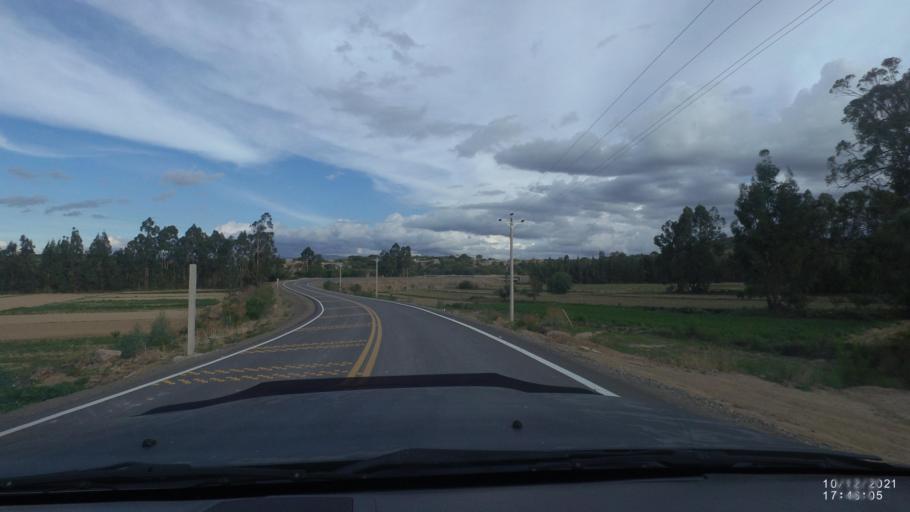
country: BO
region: Cochabamba
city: Tarata
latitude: -17.6301
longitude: -65.9965
